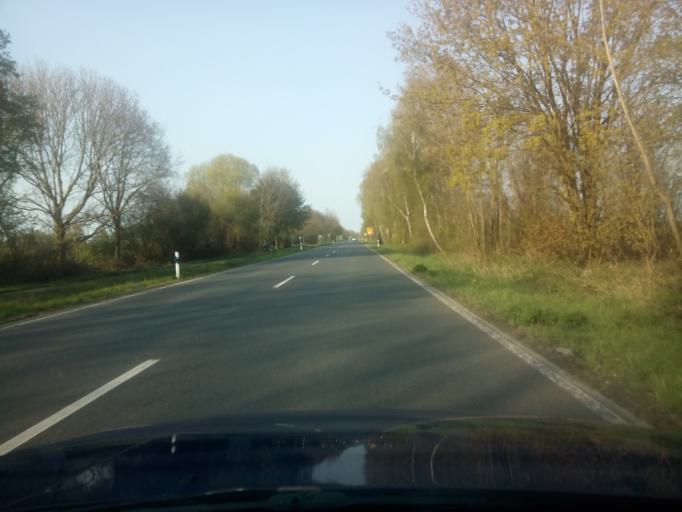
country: DE
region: Lower Saxony
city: Ritterhude
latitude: 53.1767
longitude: 8.7664
